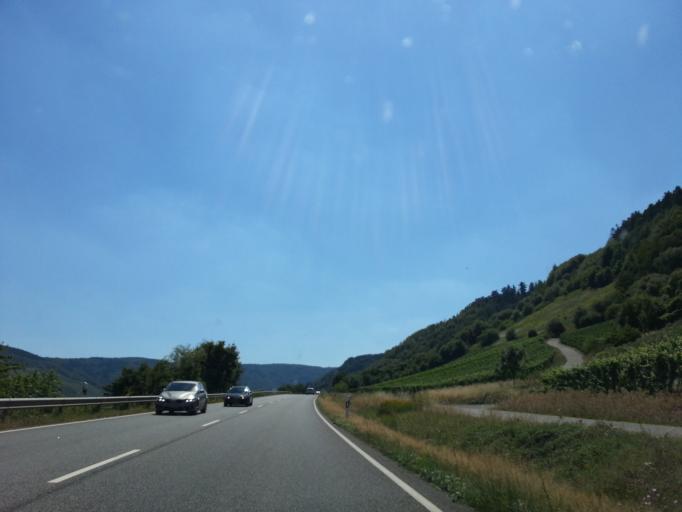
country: DE
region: Rheinland-Pfalz
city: Schleich
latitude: 49.8218
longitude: 6.8366
